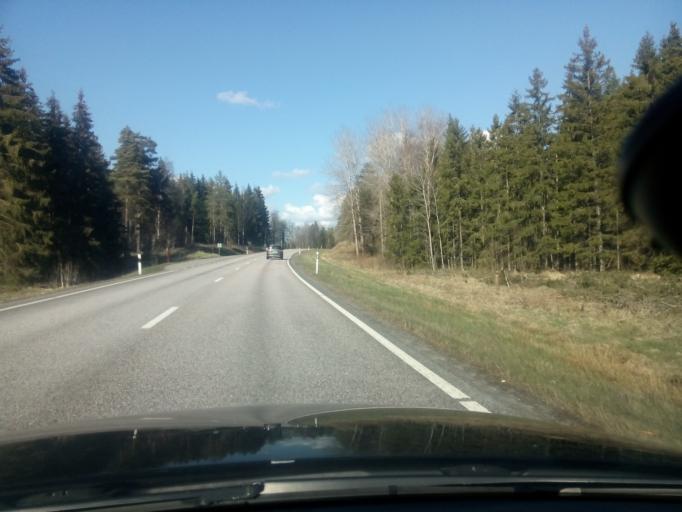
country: SE
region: Soedermanland
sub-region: Strangnas Kommun
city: Akers Styckebruk
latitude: 59.2635
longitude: 16.9492
